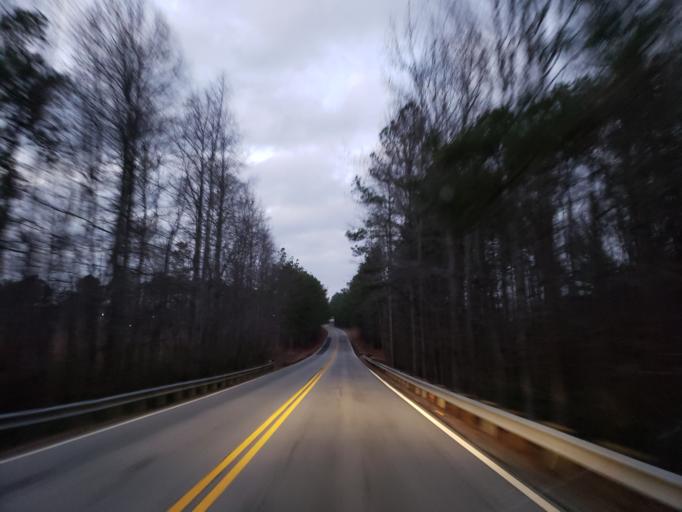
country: US
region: Georgia
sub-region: Carroll County
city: Temple
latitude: 33.7597
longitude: -85.0421
